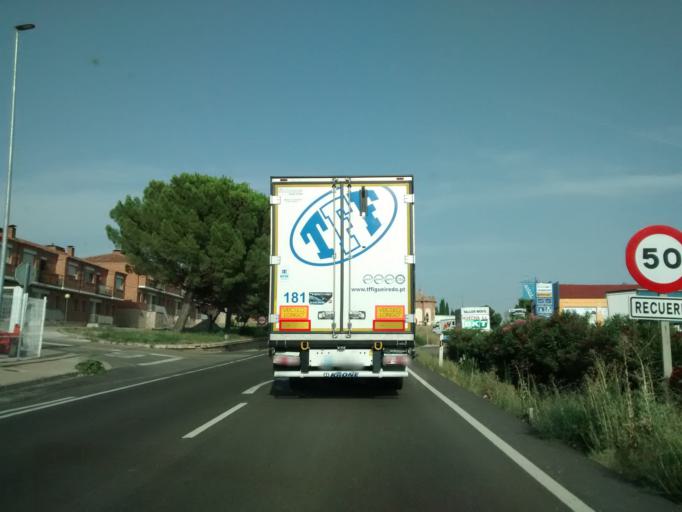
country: ES
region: Aragon
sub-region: Provincia de Zaragoza
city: Borja
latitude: 41.8317
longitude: -1.5195
